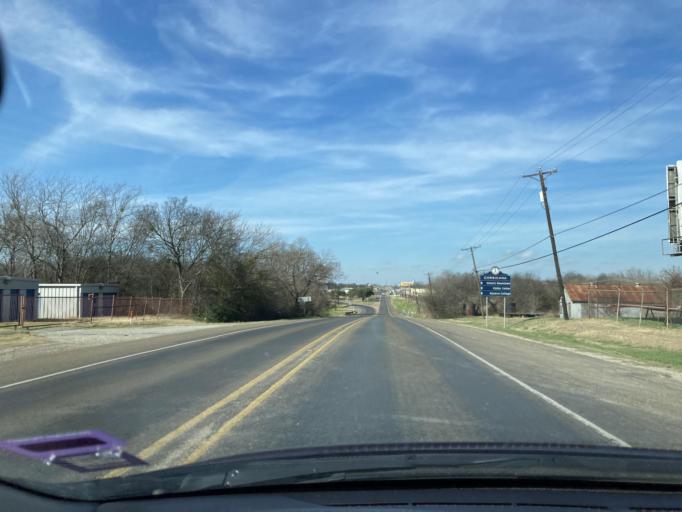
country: US
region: Texas
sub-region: Navarro County
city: Corsicana
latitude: 32.0813
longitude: -96.4504
